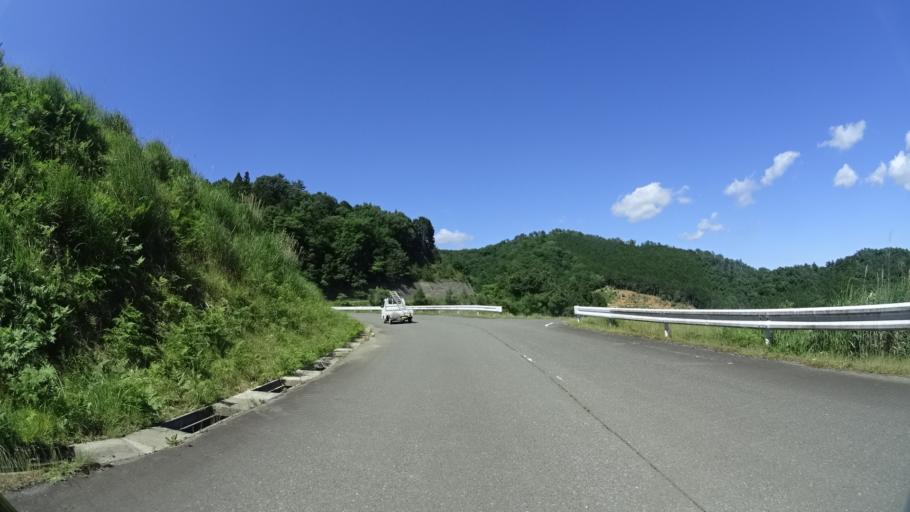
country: JP
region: Kyoto
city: Fukuchiyama
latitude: 35.3873
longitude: 135.0690
